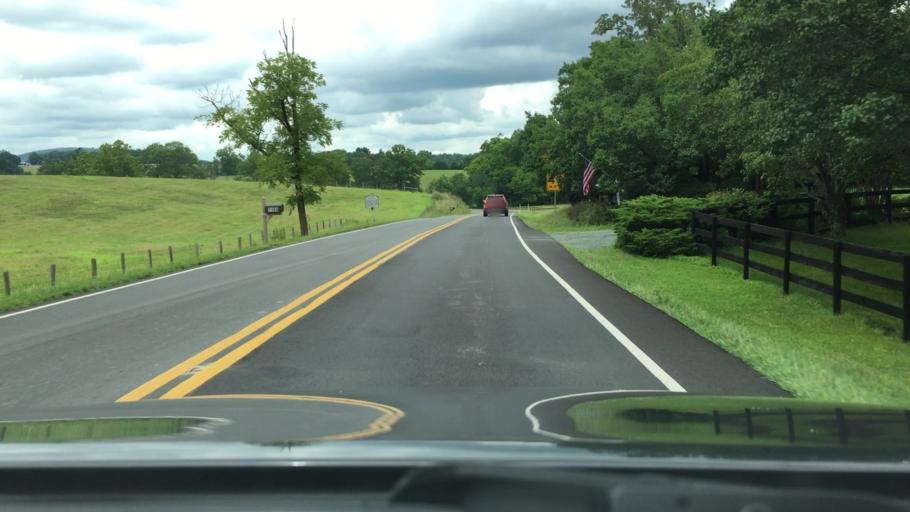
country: US
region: Virginia
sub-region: Orange County
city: Gordonsville
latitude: 38.1039
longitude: -78.2549
